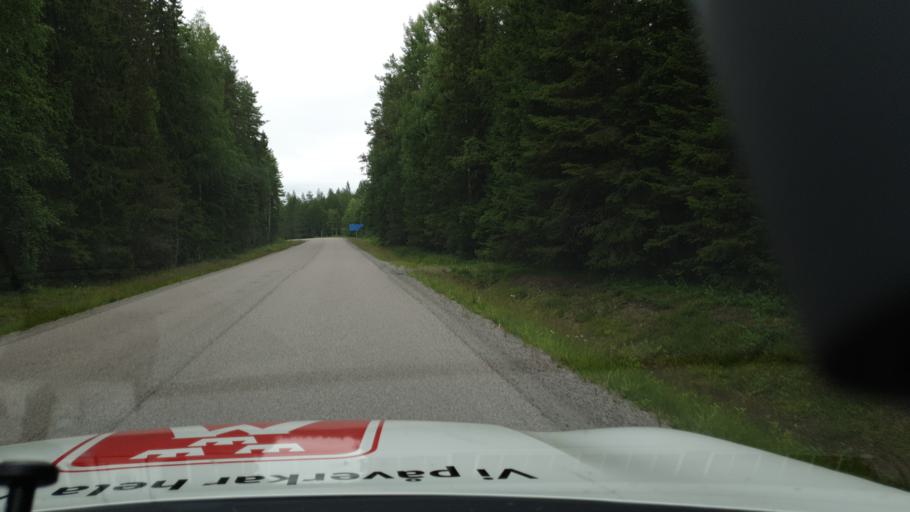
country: SE
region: Vaesterbotten
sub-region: Umea Kommun
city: Ersmark
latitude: 63.9436
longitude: 20.3044
